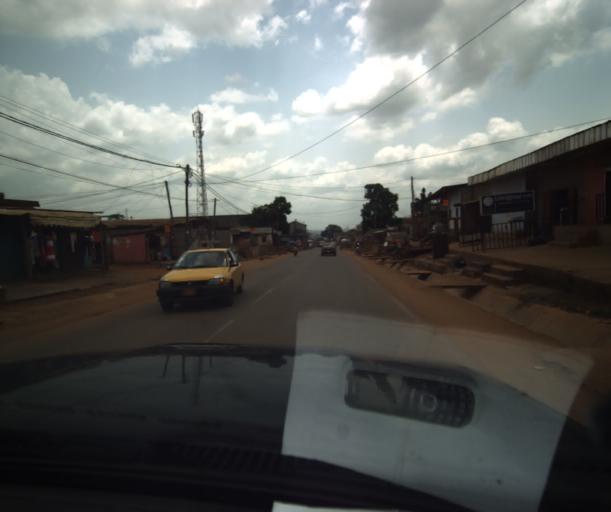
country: CM
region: Centre
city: Yaounde
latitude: 3.8329
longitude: 11.4715
